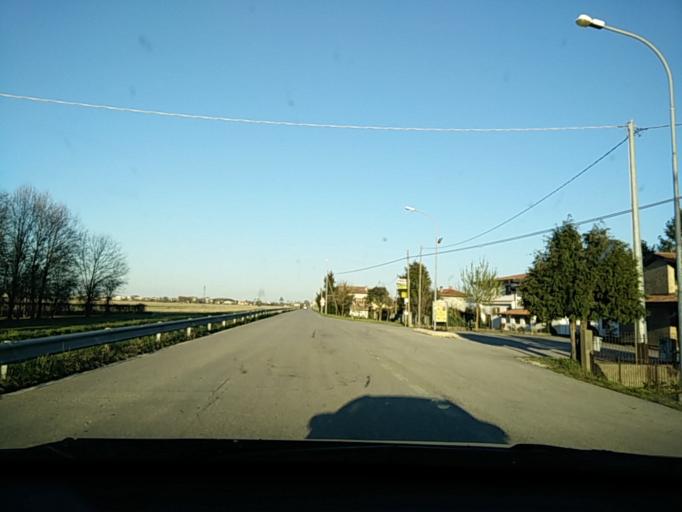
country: IT
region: Veneto
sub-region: Provincia di Venezia
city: Musile di Piave
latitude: 45.6051
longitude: 12.5352
